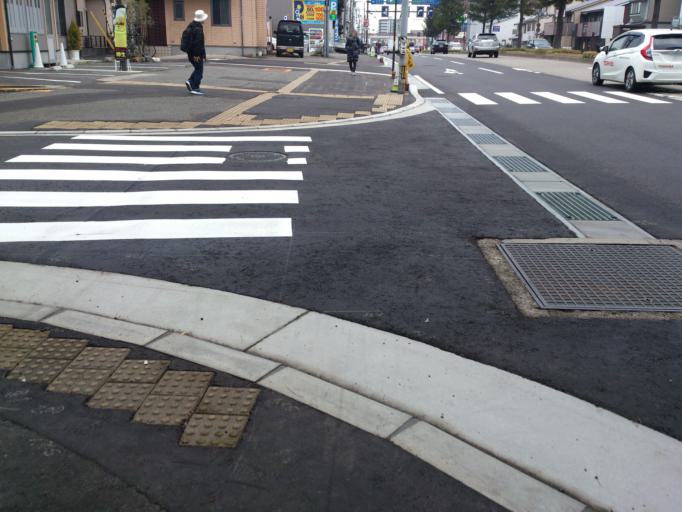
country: JP
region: Ishikawa
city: Kanazawa-shi
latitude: 36.5749
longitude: 136.6456
